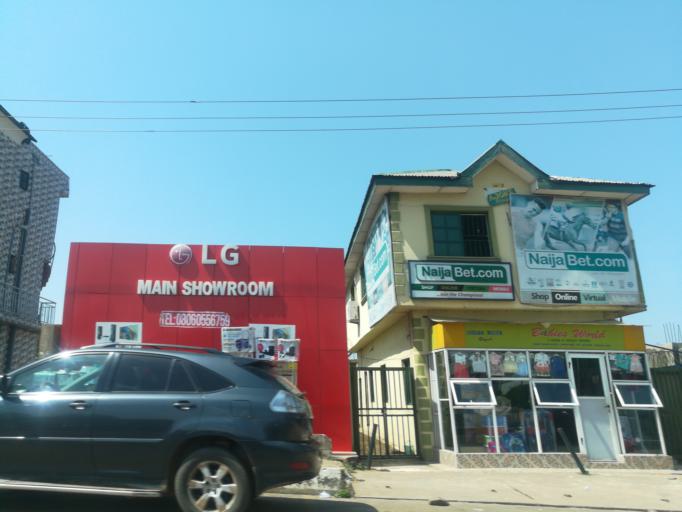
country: NG
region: Ogun
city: Abeokuta
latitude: 7.1386
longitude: 3.3345
